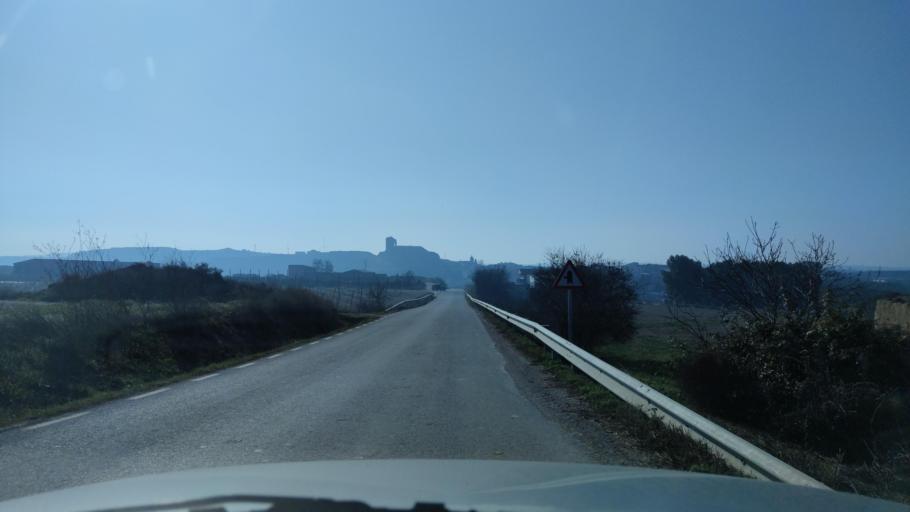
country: ES
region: Catalonia
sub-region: Provincia de Lleida
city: Torrebesses
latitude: 41.4634
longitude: 0.5653
